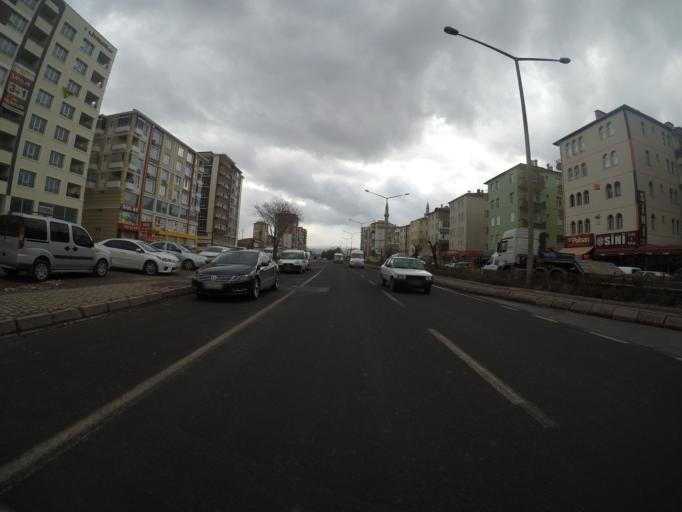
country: TR
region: Kayseri
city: Melikgazi
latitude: 38.7549
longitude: 35.4684
